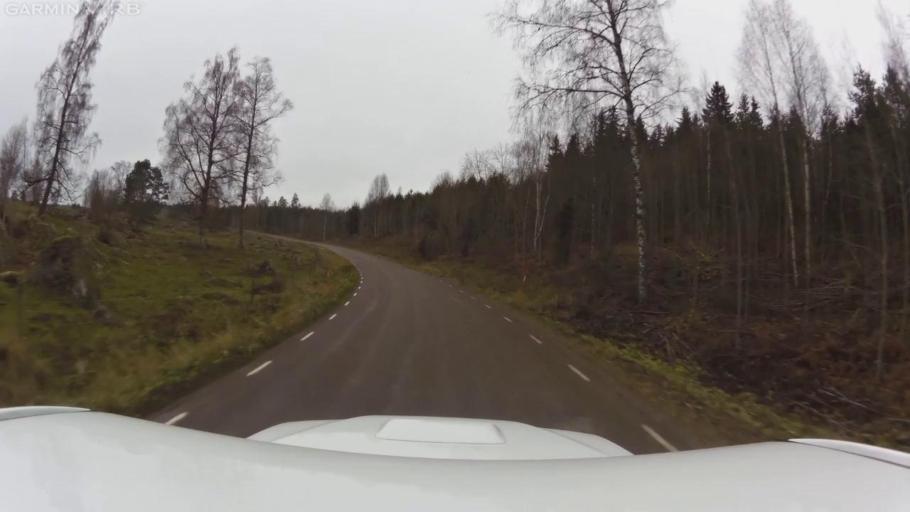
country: SE
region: OEstergoetland
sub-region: Mjolby Kommun
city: Mantorp
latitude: 58.1563
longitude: 15.3905
